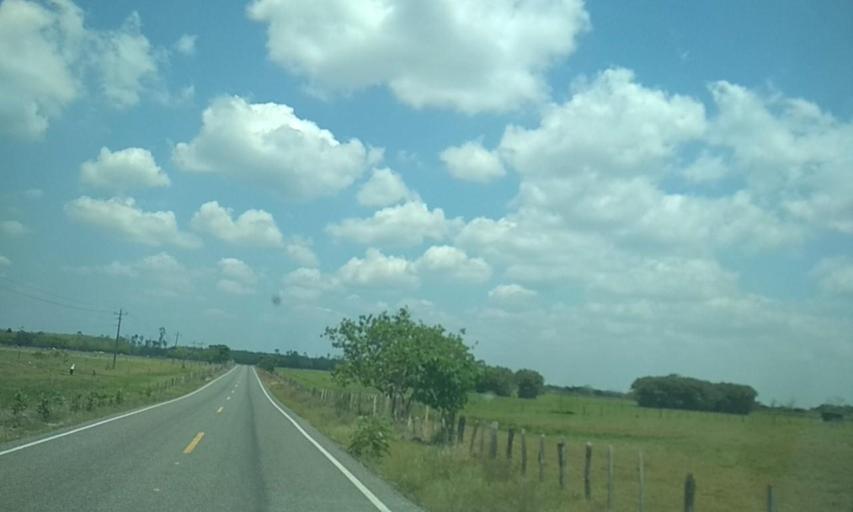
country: MX
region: Tabasco
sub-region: Huimanguillo
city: Huapacal 1ra. Seccion
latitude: 17.7530
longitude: -93.7184
